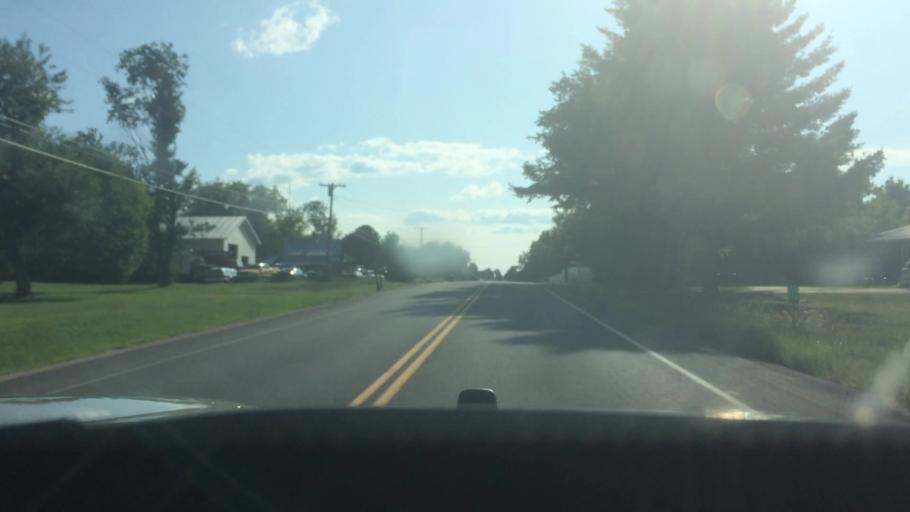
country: US
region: New York
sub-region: Franklin County
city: Malone
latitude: 44.7838
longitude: -74.4885
